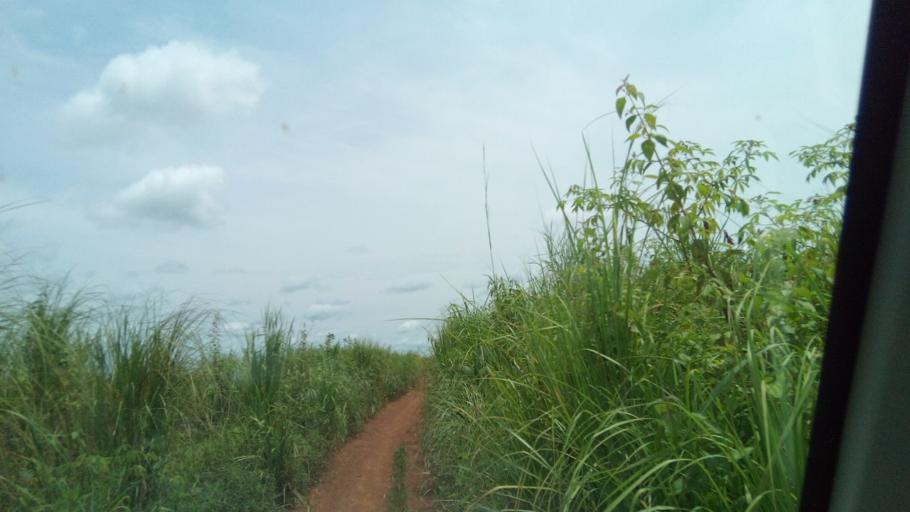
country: AO
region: Zaire
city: Mbanza Congo
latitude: -5.7917
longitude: 13.9922
